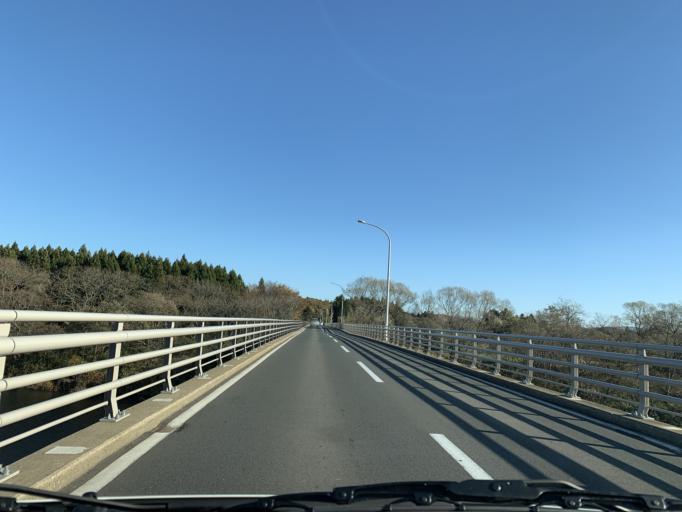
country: JP
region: Iwate
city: Kitakami
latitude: 39.2525
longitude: 141.1153
